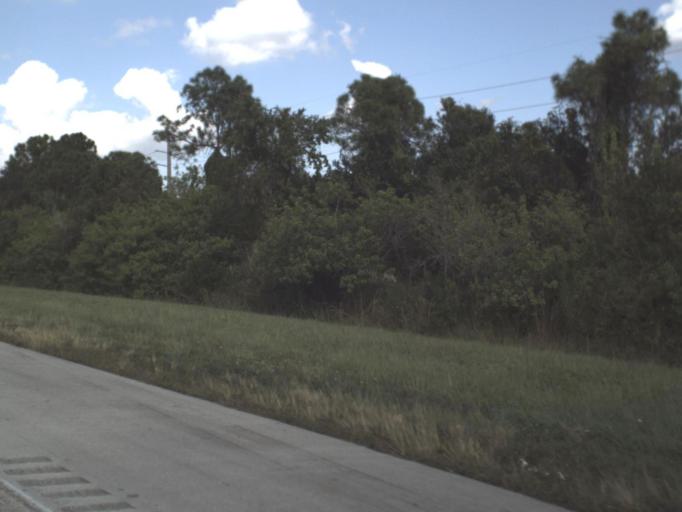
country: US
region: Florida
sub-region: Martin County
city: Palm City
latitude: 27.1305
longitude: -80.2836
